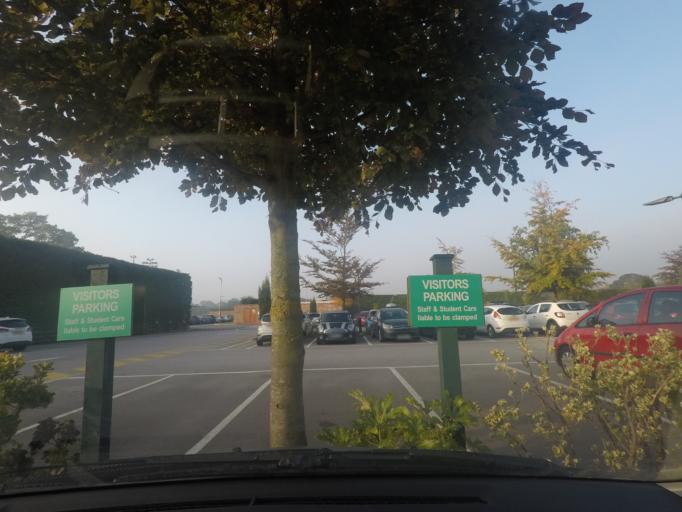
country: GB
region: England
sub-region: City and Borough of Leeds
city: Walton
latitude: 54.0265
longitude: -1.2963
